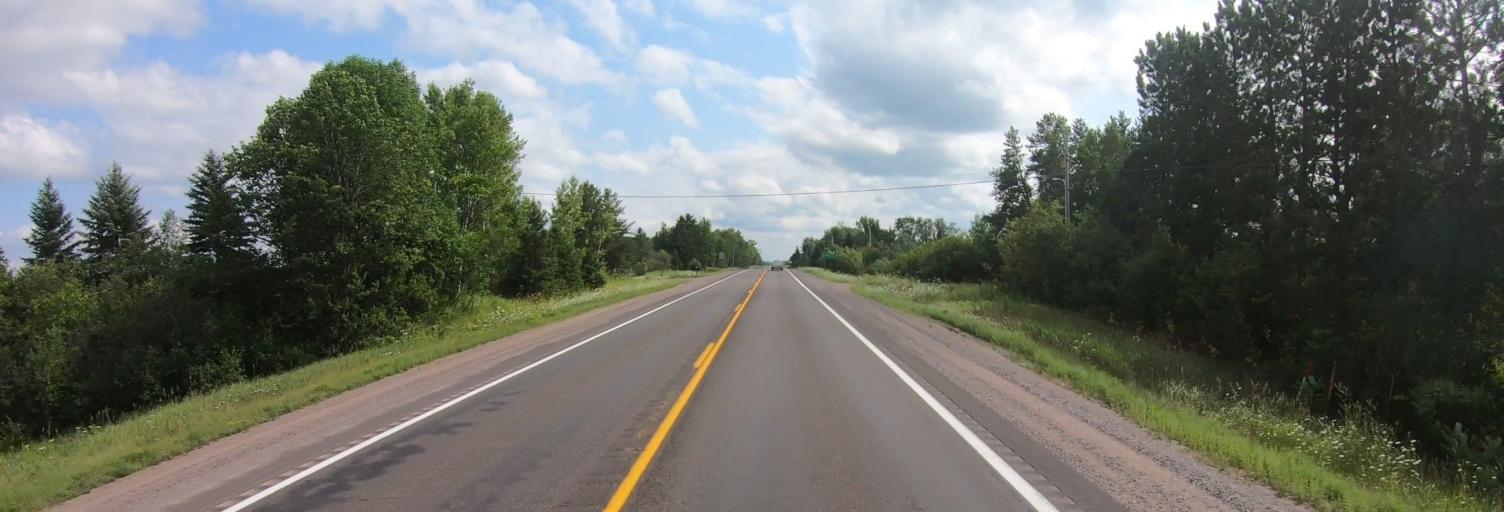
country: US
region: Michigan
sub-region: Ontonagon County
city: Ontonagon
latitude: 46.5812
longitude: -89.1785
